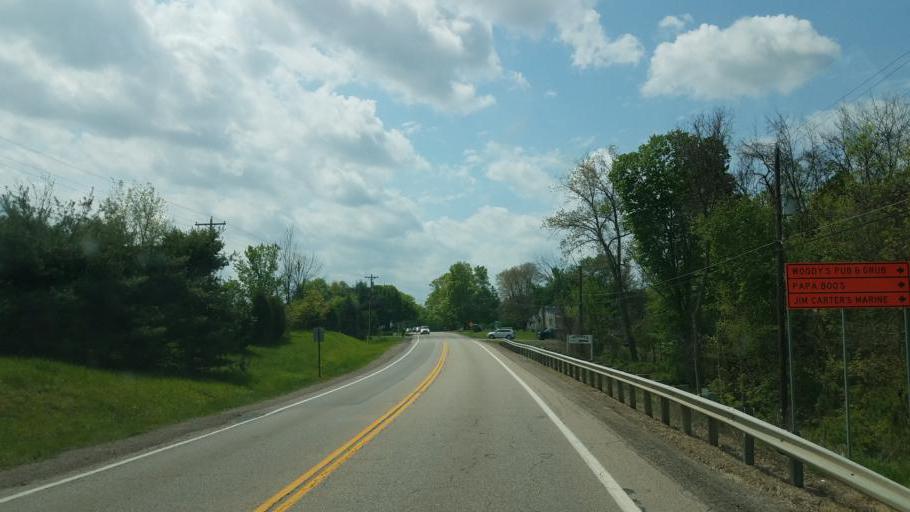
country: US
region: Ohio
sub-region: Perry County
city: Thornport
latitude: 39.9308
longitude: -82.4092
